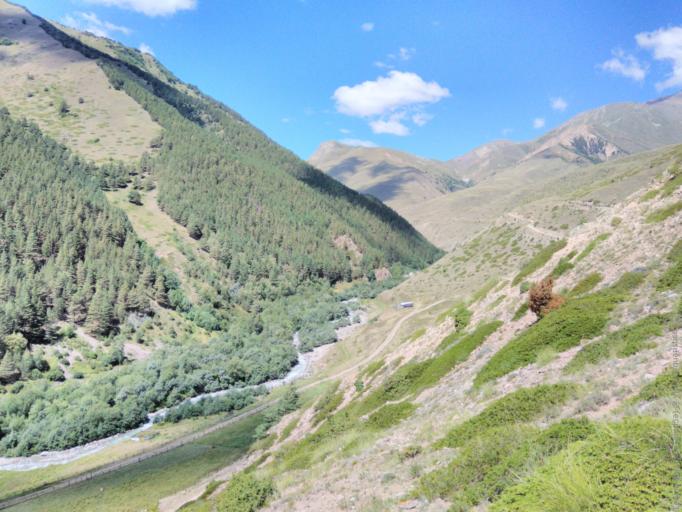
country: RU
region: Kabardino-Balkariya
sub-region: El'brusskiy Rayon
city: El'brus
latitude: 43.3471
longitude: 42.7506
